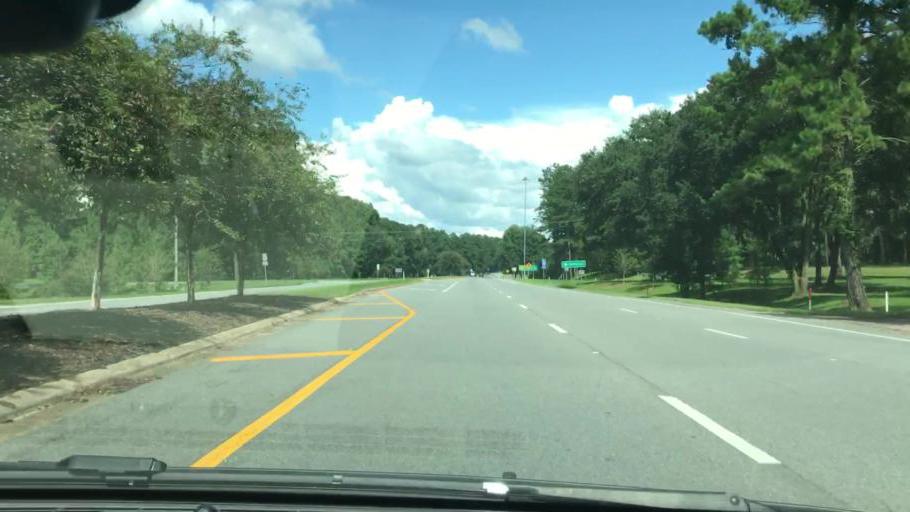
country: US
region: Florida
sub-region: Leon County
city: Tallahassee
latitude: 30.4877
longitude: -84.1576
